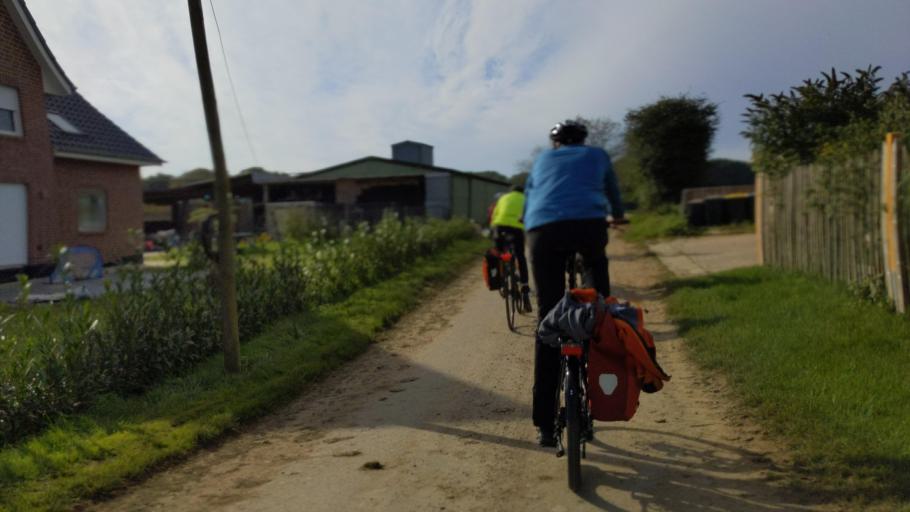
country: DE
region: Schleswig-Holstein
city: Zarpen
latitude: 53.8829
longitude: 10.4997
